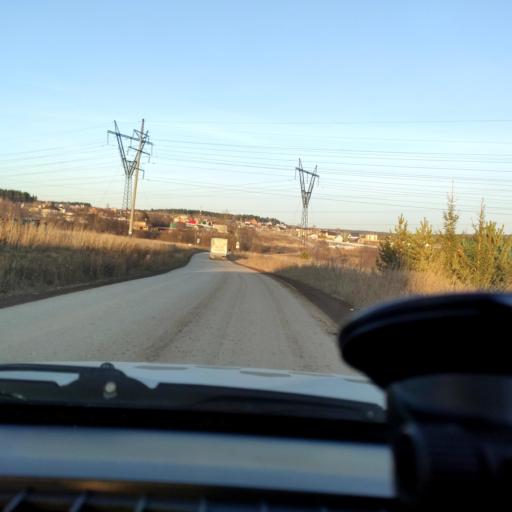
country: RU
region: Perm
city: Ferma
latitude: 57.9495
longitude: 56.3631
